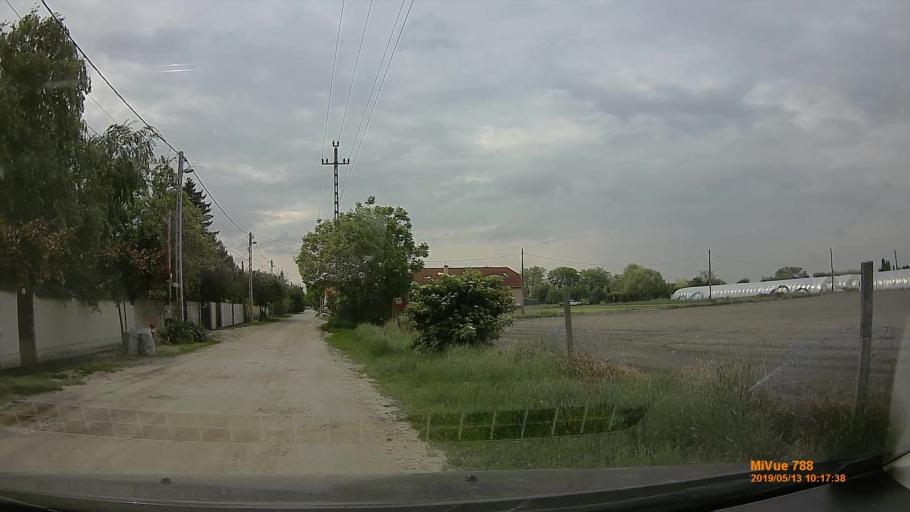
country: HU
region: Budapest
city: Budapest XXIII. keruelet
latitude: 47.3975
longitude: 19.0888
